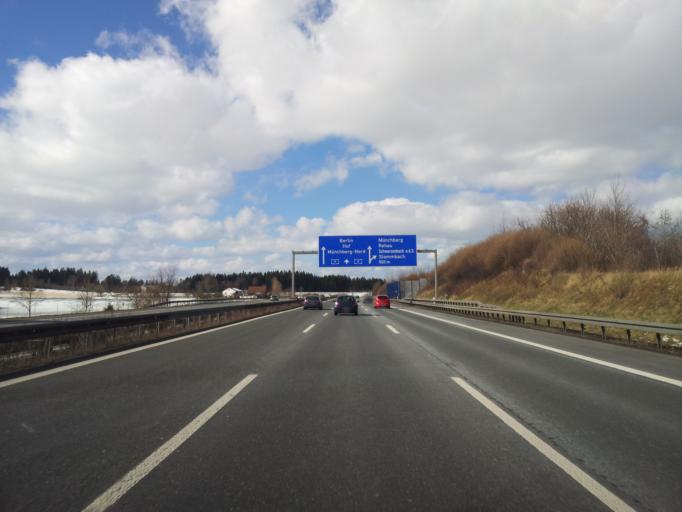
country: DE
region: Bavaria
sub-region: Upper Franconia
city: Munchberg
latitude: 50.1608
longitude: 11.7476
